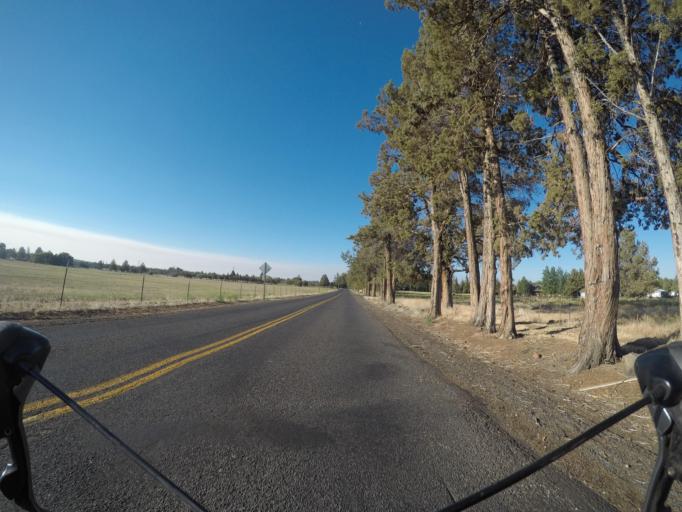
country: US
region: Oregon
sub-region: Deschutes County
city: Redmond
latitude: 44.2644
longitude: -121.2452
